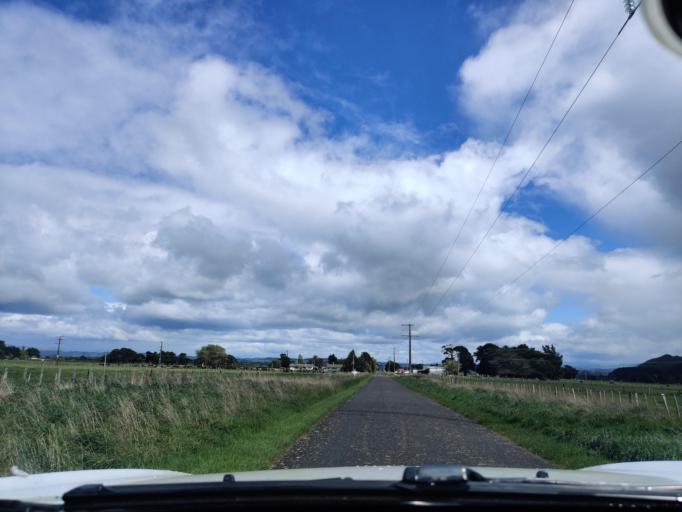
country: NZ
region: Manawatu-Wanganui
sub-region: Palmerston North City
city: Palmerston North
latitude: -40.3097
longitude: 175.8590
